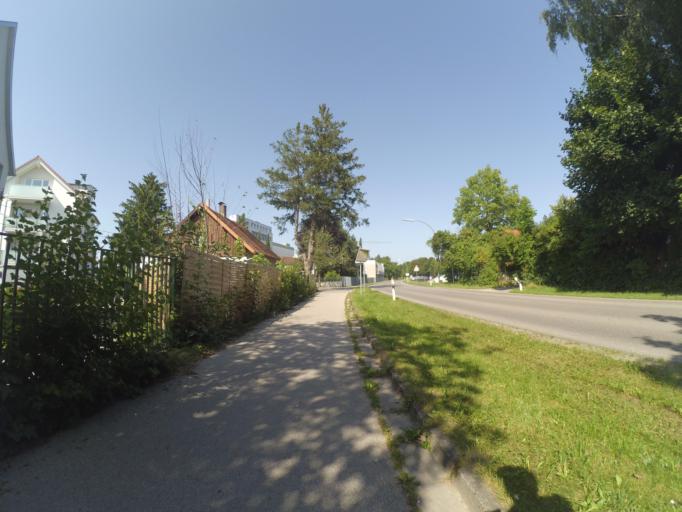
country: DE
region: Bavaria
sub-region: Swabia
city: Buchloe
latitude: 48.0351
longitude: 10.7153
